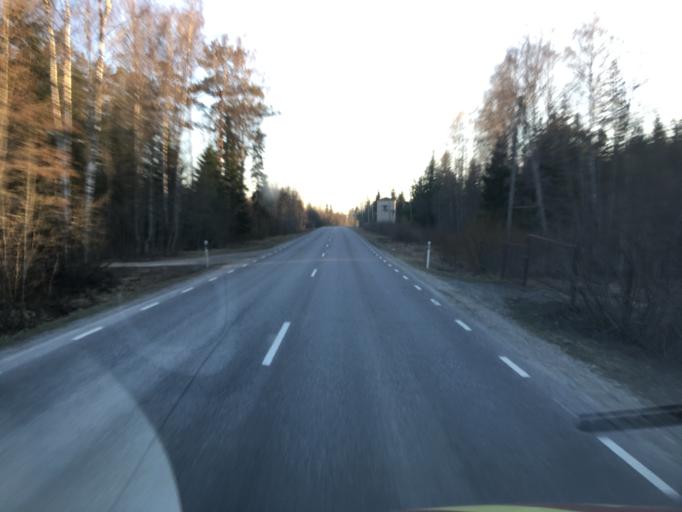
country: EE
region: Raplamaa
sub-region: Rapla vald
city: Rapla
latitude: 58.9940
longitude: 24.8418
